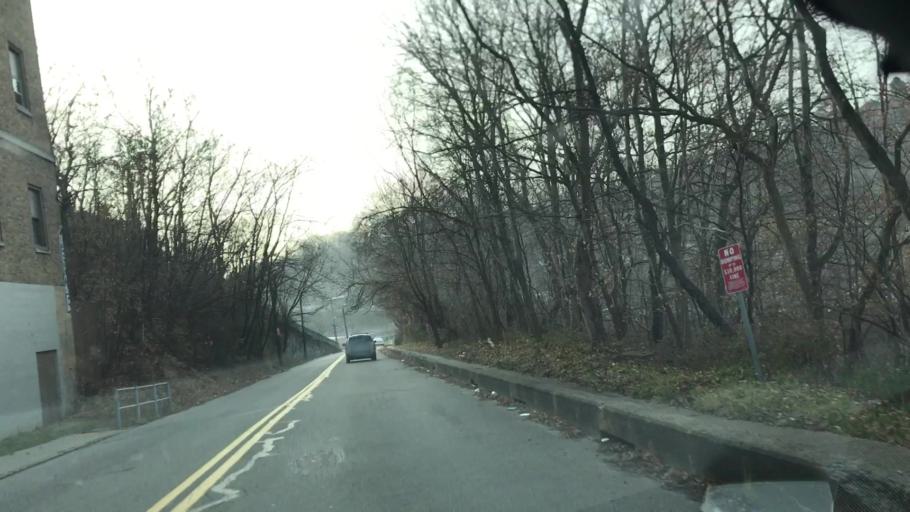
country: US
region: Pennsylvania
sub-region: Allegheny County
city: Mount Oliver
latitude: 40.4172
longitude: -80.0137
